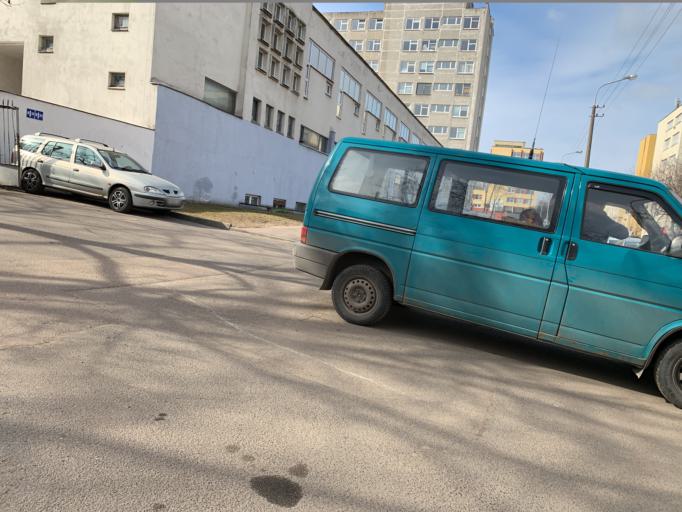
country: BY
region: Minsk
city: Minsk
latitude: 53.9123
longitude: 27.6022
